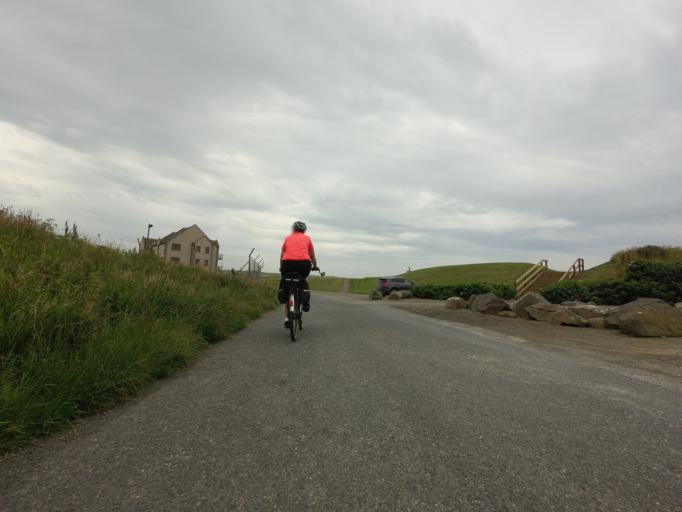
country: GB
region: Scotland
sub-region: Aberdeenshire
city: Whitehills
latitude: 57.6813
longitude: -2.5756
